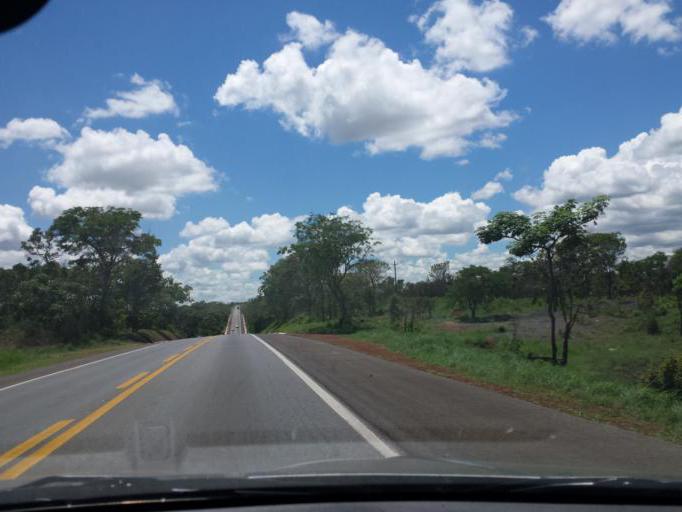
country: BR
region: Goias
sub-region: Cristalina
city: Cristalina
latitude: -16.6570
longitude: -47.7287
